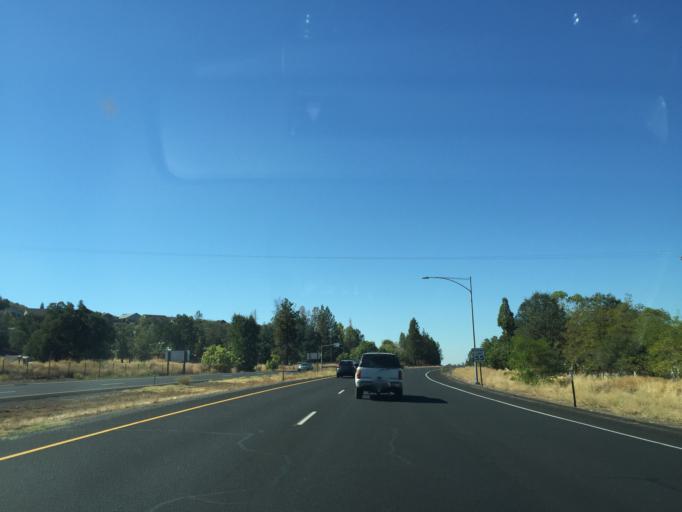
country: US
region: California
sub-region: Tuolumne County
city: Mono Vista
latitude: 37.9961
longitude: -120.2682
